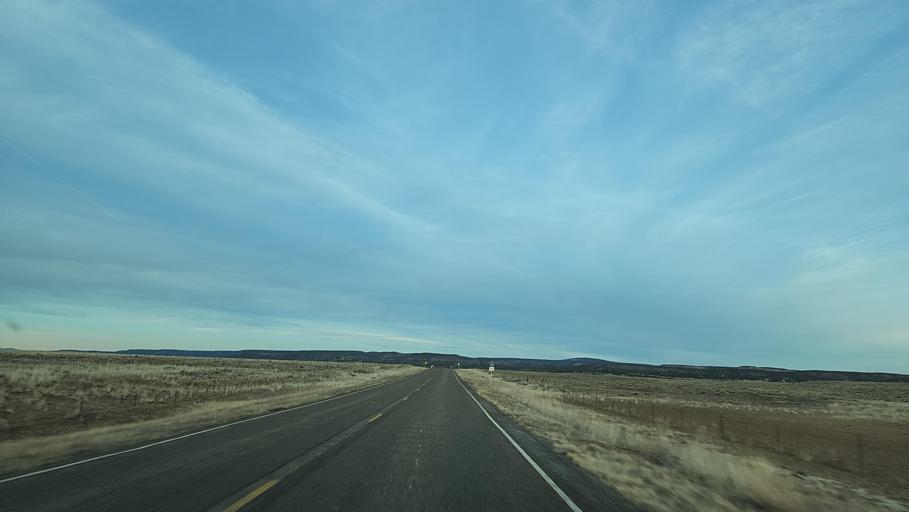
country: US
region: New Mexico
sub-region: Cibola County
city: Grants
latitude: 34.7019
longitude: -108.0310
